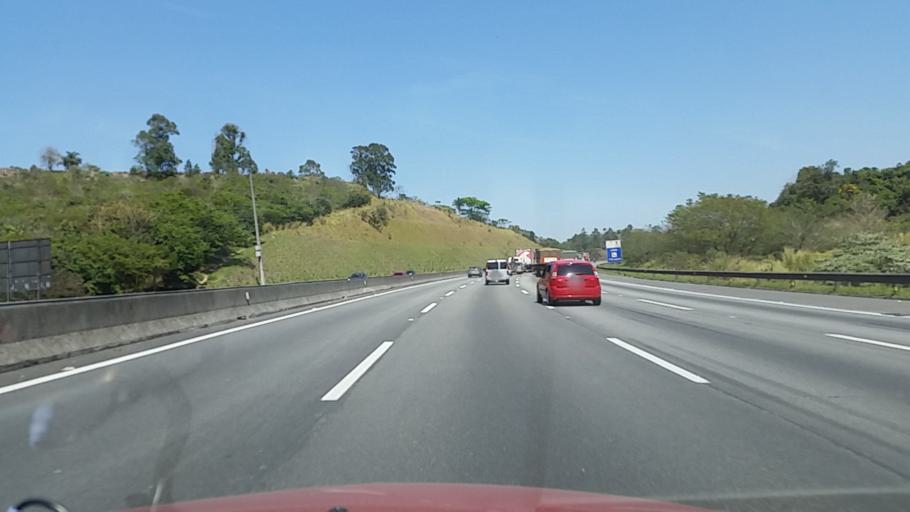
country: BR
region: Sao Paulo
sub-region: Taboao Da Serra
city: Taboao da Serra
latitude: -23.6084
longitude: -46.8149
